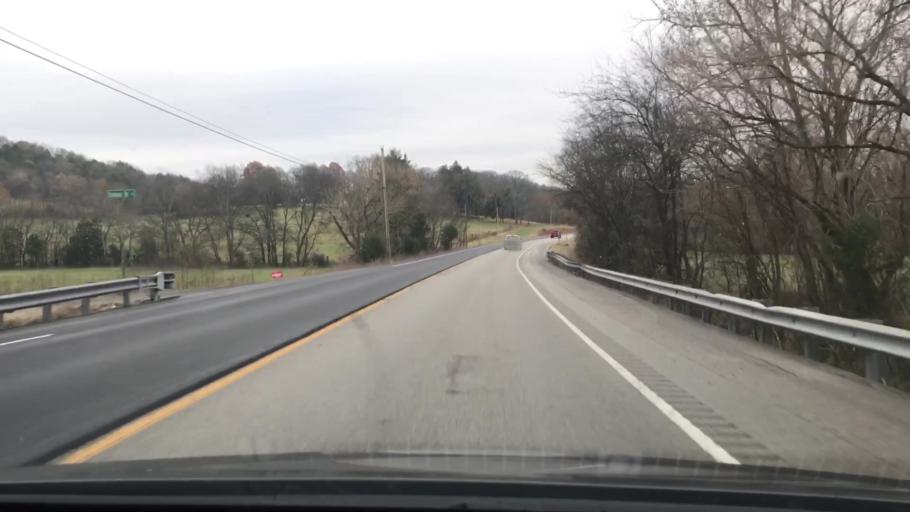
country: US
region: Tennessee
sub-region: Smith County
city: Carthage
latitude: 36.3182
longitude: -86.0117
